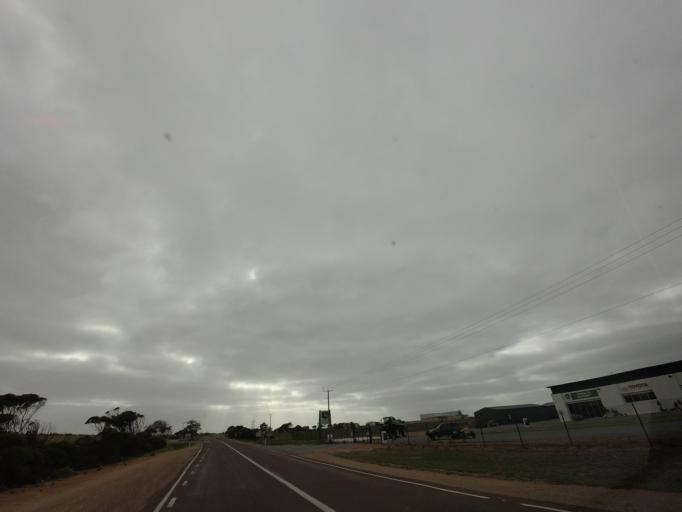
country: AU
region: South Australia
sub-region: Ceduna
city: Ceduna
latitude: -32.1228
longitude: 133.6966
